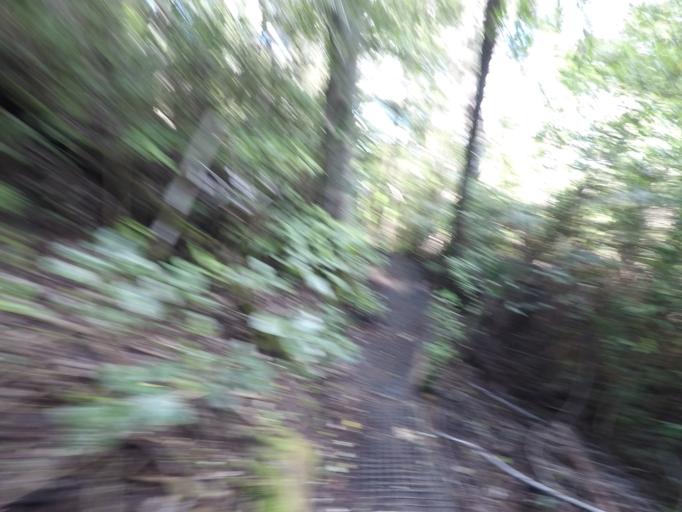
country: NZ
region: Auckland
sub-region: Auckland
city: Rothesay Bay
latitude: -36.7371
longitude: 174.7069
